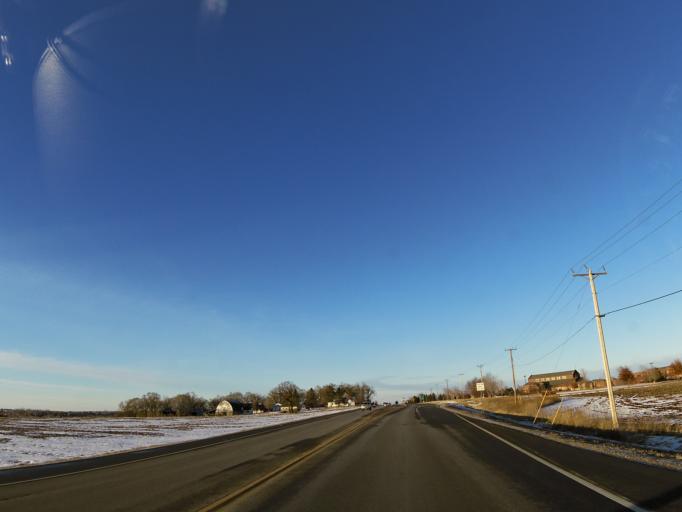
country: US
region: Minnesota
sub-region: Washington County
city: Woodbury
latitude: 44.8857
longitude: -92.9033
